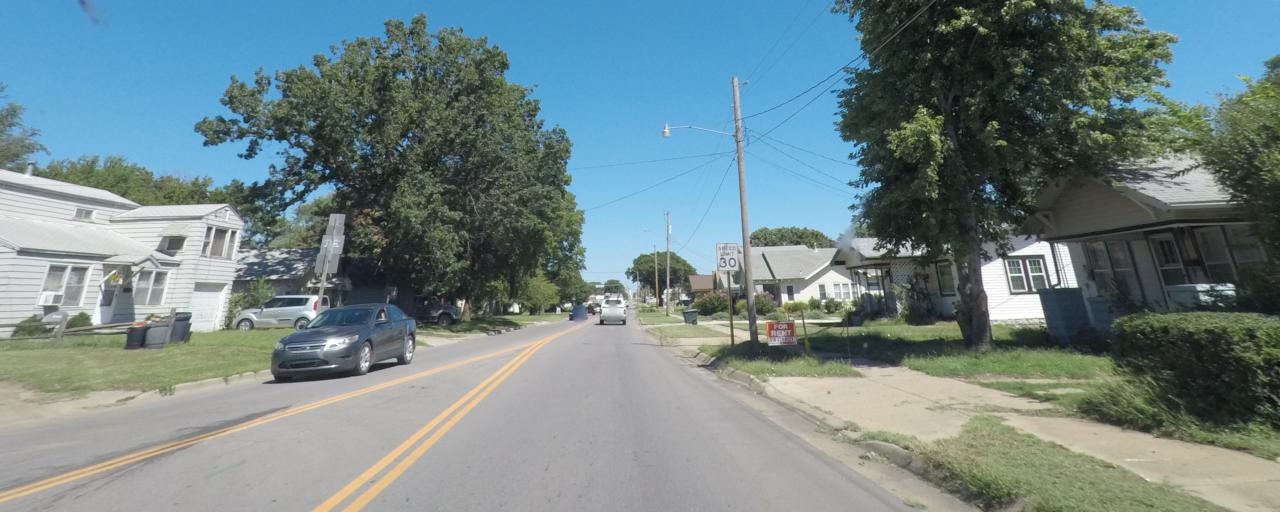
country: US
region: Kansas
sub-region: Sumner County
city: Wellington
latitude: 37.2765
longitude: -97.3942
